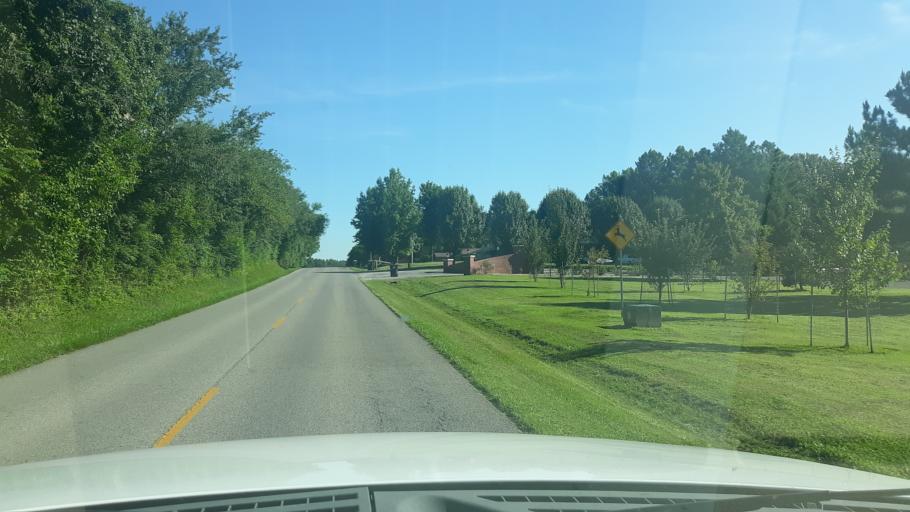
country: US
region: Illinois
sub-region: Saline County
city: Harrisburg
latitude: 37.7300
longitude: -88.5688
